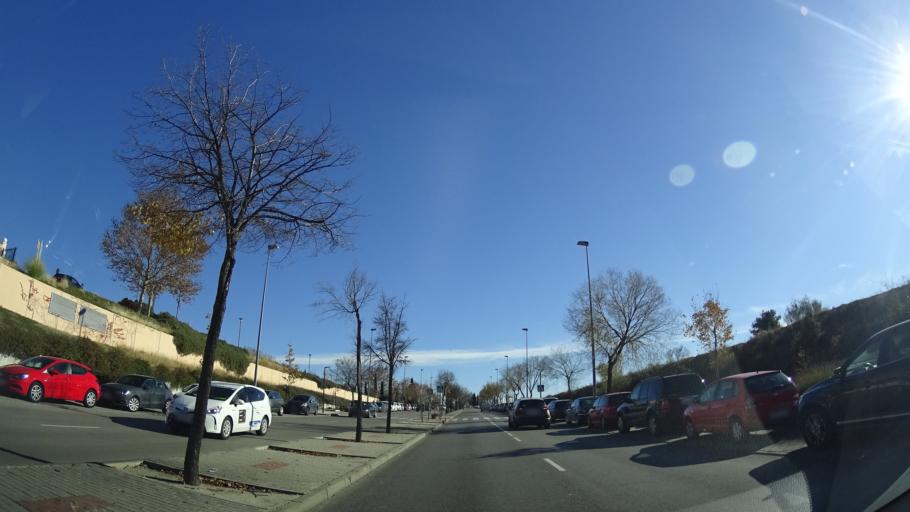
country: ES
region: Madrid
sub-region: Provincia de Madrid
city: Las Rozas de Madrid
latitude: 40.5177
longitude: -3.9034
